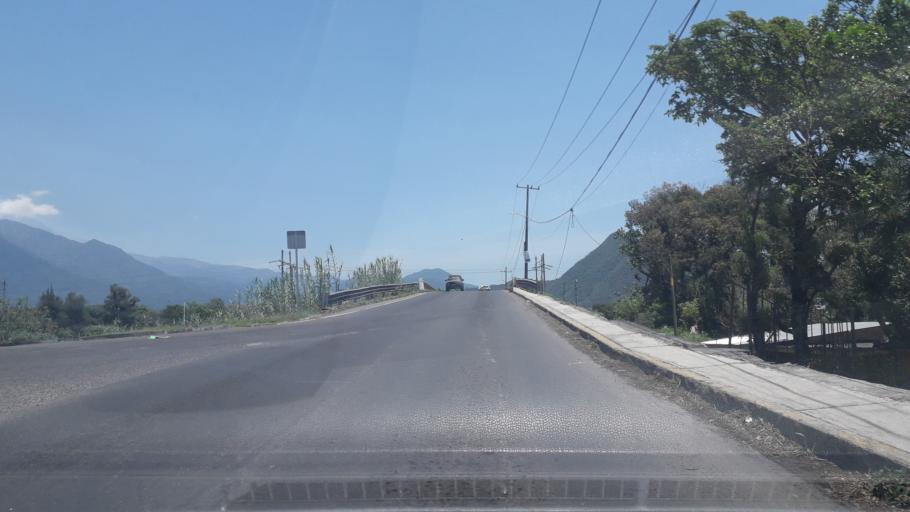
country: MX
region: Veracruz
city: Jalapilla
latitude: 18.8306
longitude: -97.0905
